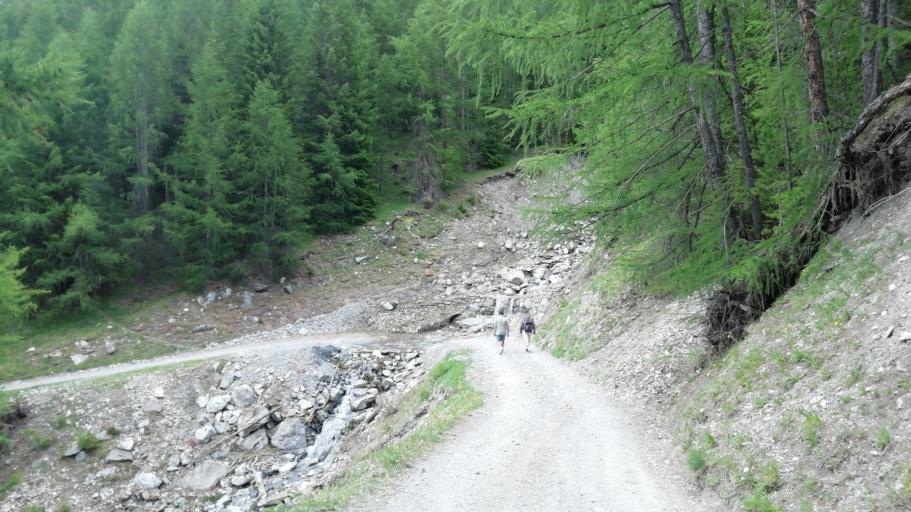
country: IT
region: Lombardy
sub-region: Provincia di Sondrio
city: Sant'Antonio
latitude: 46.4800
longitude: 10.4645
